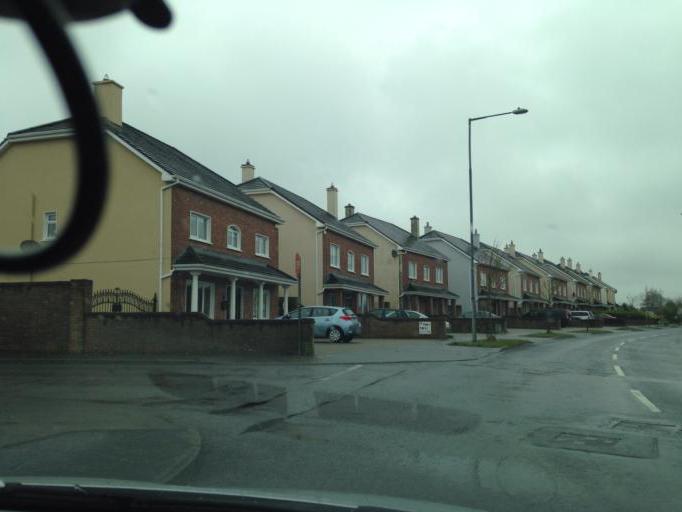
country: IE
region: Connaught
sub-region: County Galway
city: Gaillimh
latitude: 53.2731
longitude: -9.1004
